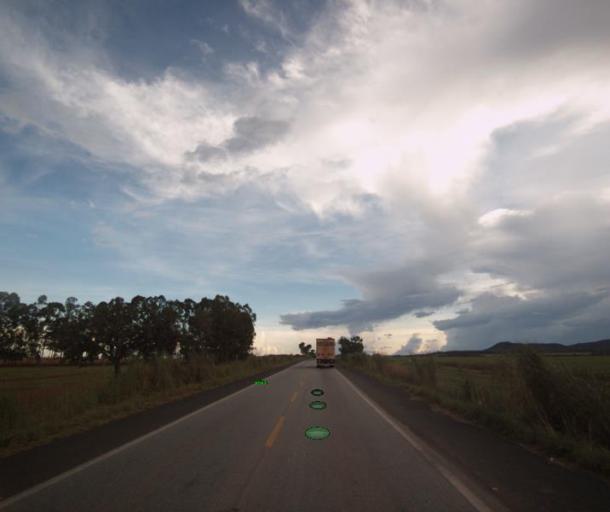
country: BR
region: Goias
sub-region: Uruacu
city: Uruacu
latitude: -14.1404
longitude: -49.1150
